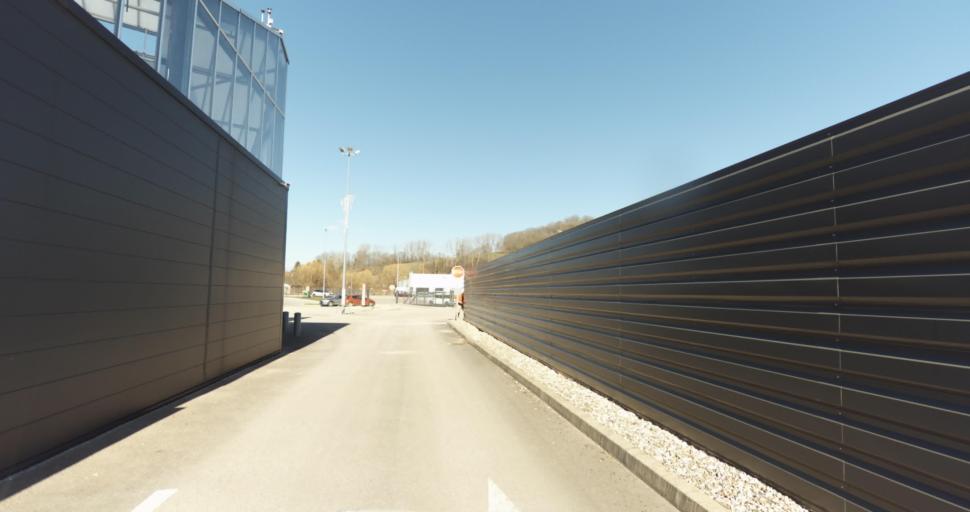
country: FR
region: Franche-Comte
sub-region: Departement du Jura
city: Montmorot
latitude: 46.6757
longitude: 5.5231
